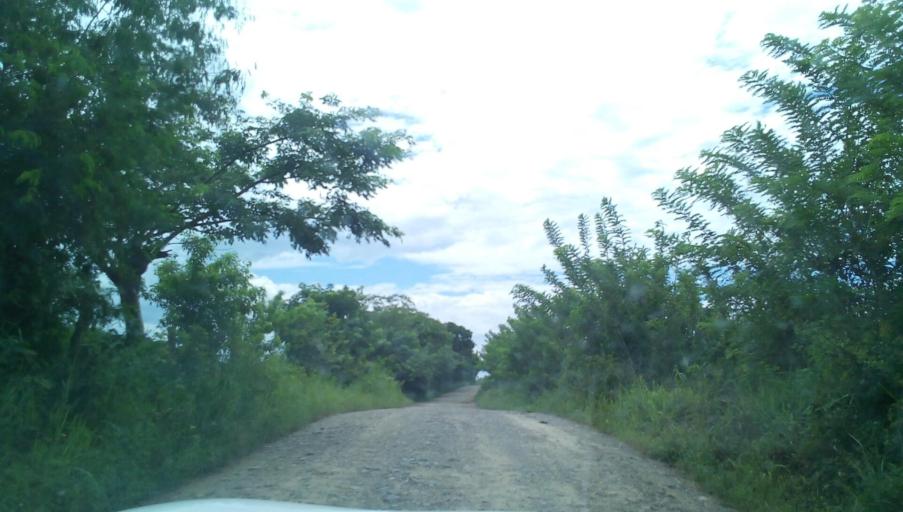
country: MX
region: Veracruz
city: Tepetzintla
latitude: 21.1460
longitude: -97.8556
